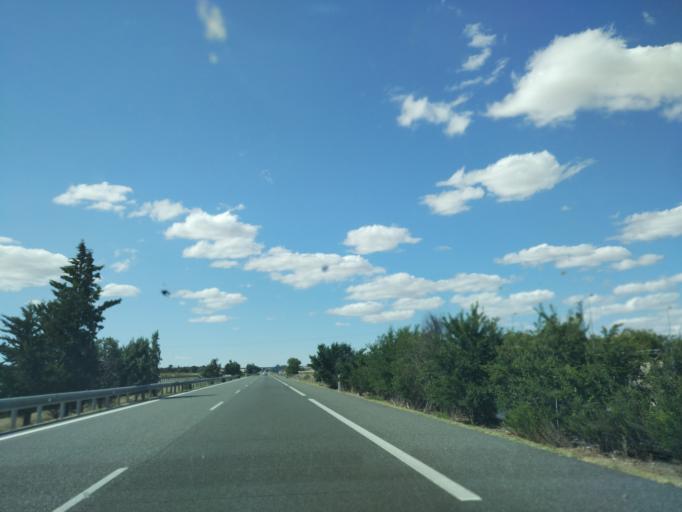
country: ES
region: Castille and Leon
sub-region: Provincia de Valladolid
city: Medina del Campo
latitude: 41.2750
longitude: -4.8883
